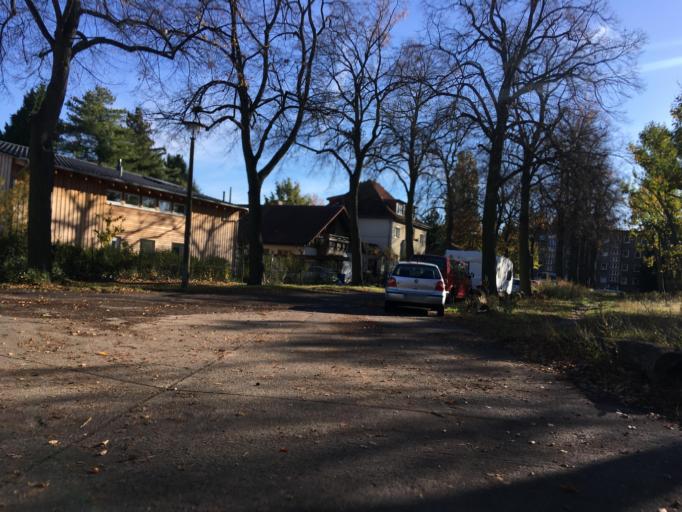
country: DE
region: Berlin
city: Friedrichshagen
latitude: 52.4520
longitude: 13.6347
